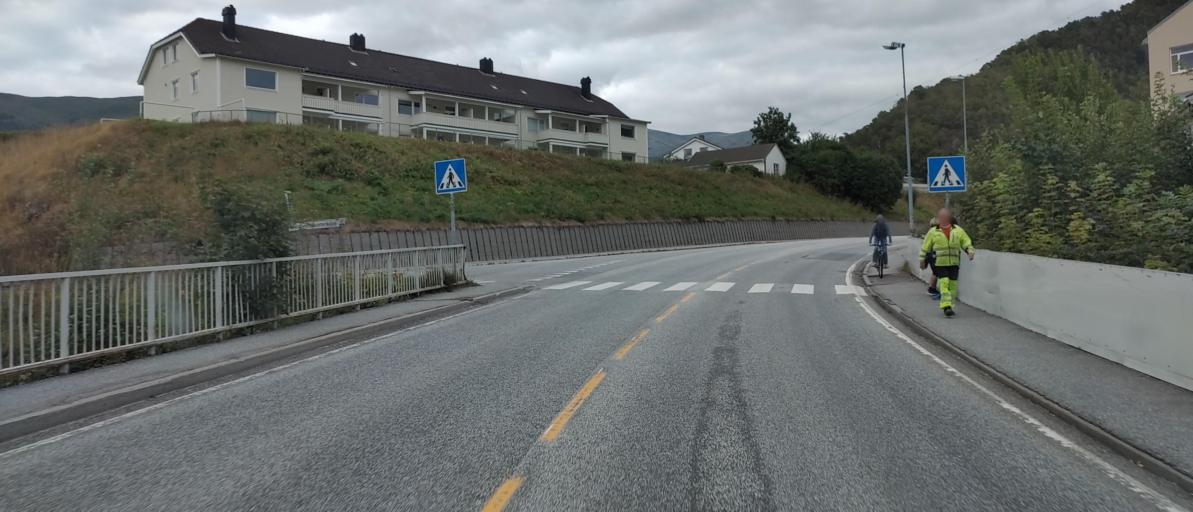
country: NO
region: More og Romsdal
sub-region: Rauma
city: Andalsnes
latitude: 62.5614
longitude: 7.6854
